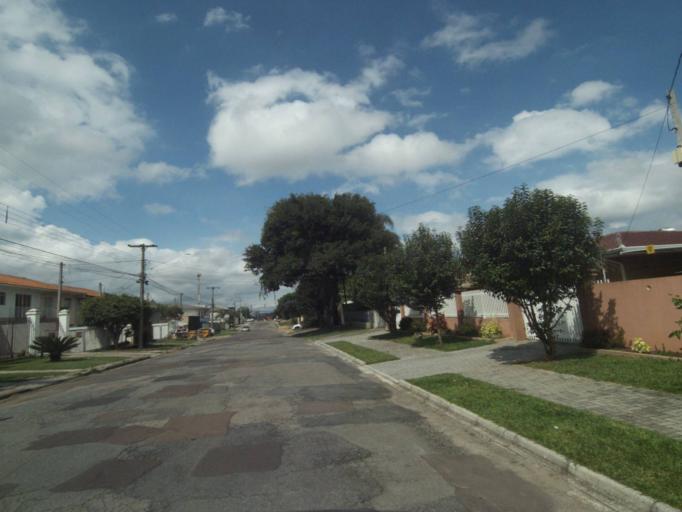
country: BR
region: Parana
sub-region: Pinhais
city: Pinhais
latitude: -25.4554
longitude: -49.2121
